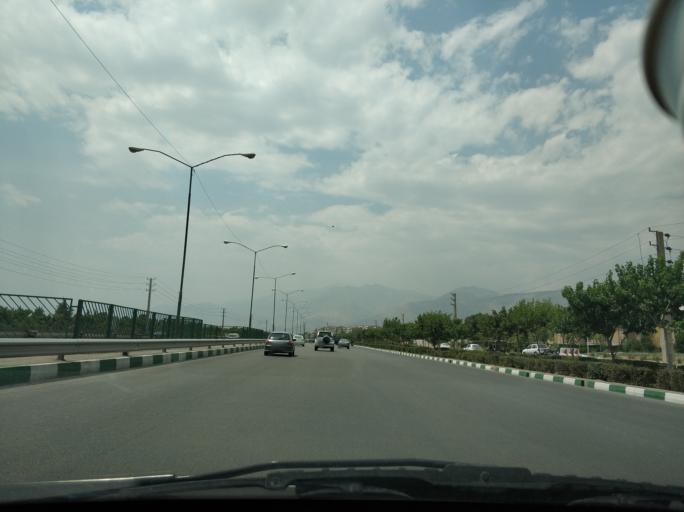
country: IR
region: Tehran
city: Tajrish
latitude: 35.7617
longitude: 51.5701
